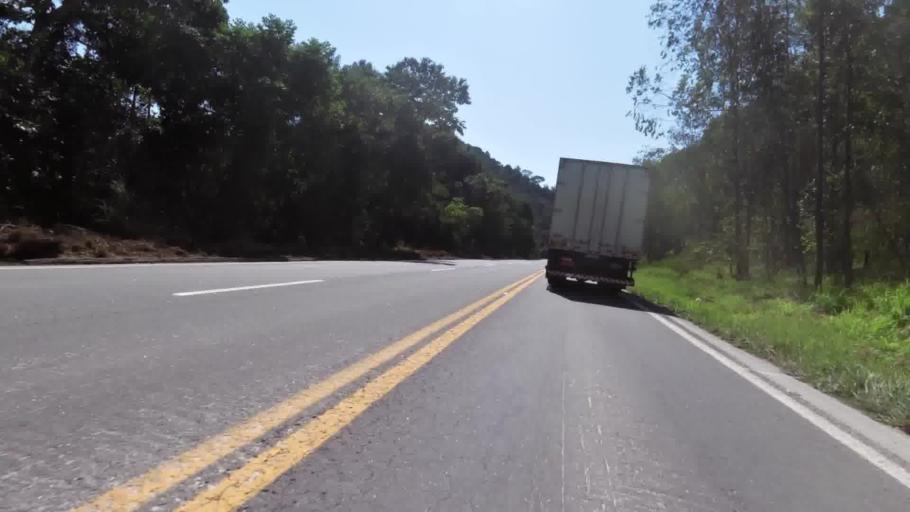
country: BR
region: Espirito Santo
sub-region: Marechal Floriano
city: Marechal Floriano
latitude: -20.4176
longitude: -40.8718
